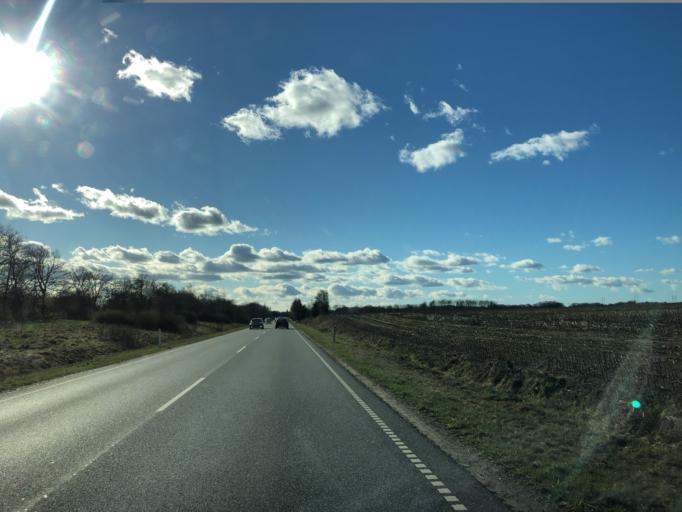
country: DK
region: Central Jutland
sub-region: Viborg Kommune
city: Bjerringbro
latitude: 56.3559
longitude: 9.5505
